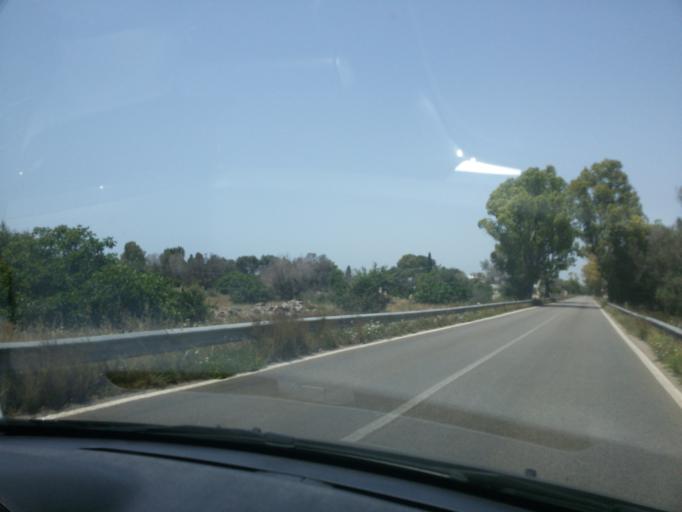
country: IT
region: Apulia
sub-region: Provincia di Lecce
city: Porto Cesareo
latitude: 40.2558
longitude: 17.9279
